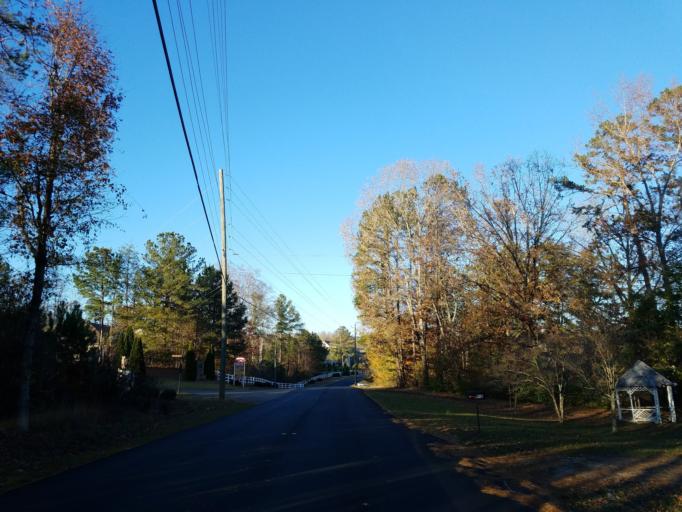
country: US
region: Georgia
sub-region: Cherokee County
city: Ball Ground
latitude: 34.3473
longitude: -84.3657
